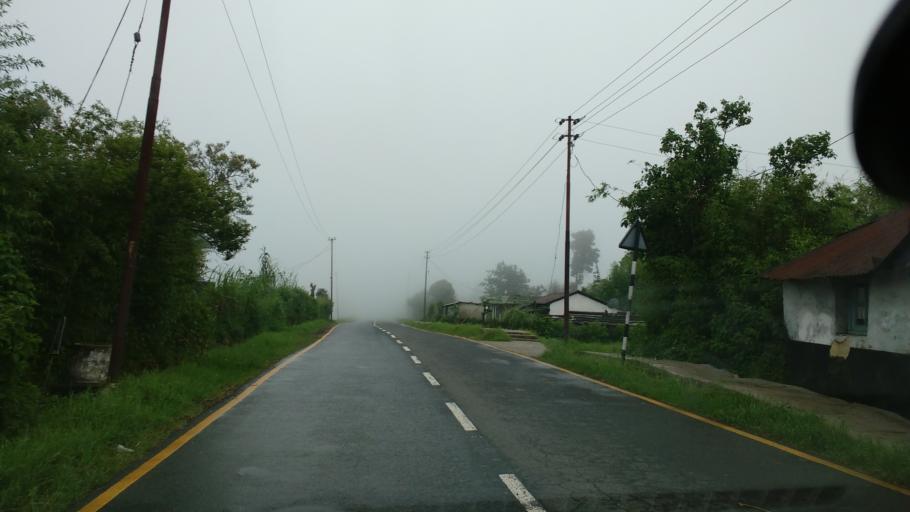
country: IN
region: Meghalaya
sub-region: East Khasi Hills
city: Cherrapunji
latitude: 25.3485
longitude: 91.7389
